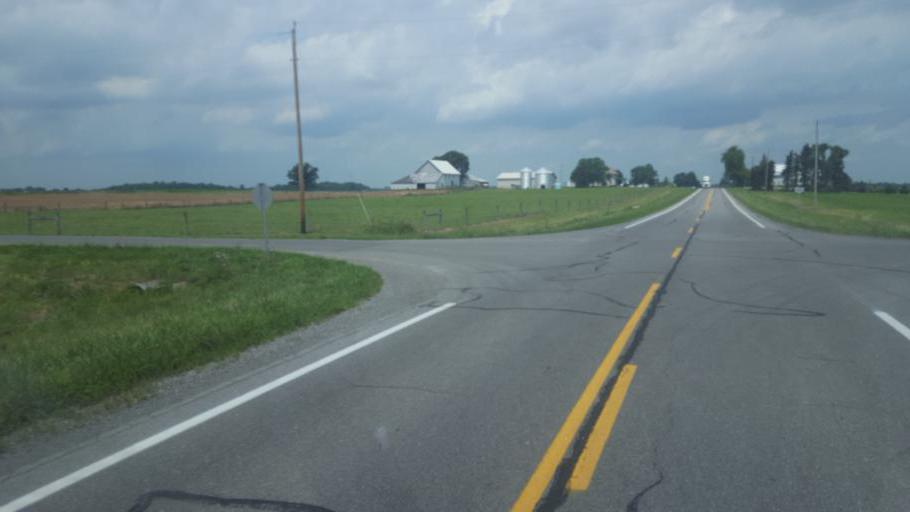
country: US
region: Ohio
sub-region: Hardin County
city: Kenton
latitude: 40.5956
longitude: -83.5936
